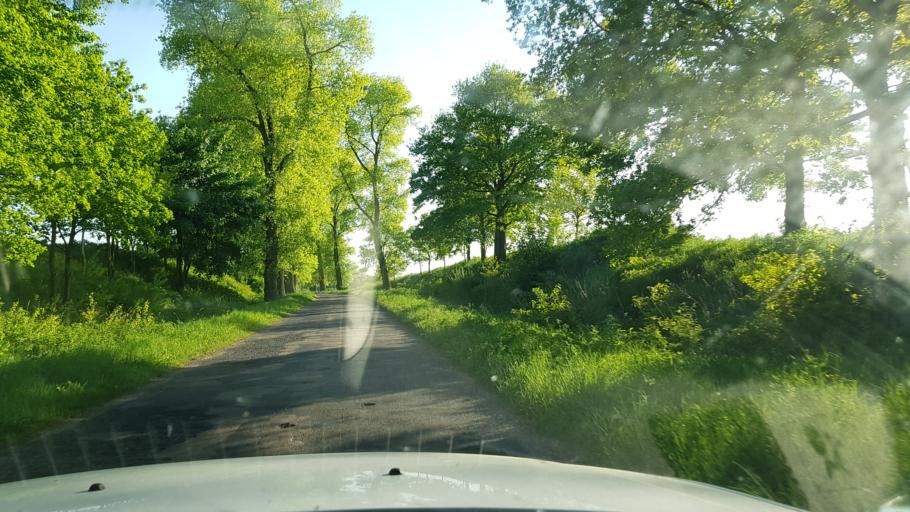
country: PL
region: West Pomeranian Voivodeship
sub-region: Powiat lobeski
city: Dobra
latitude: 53.5931
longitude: 15.3295
